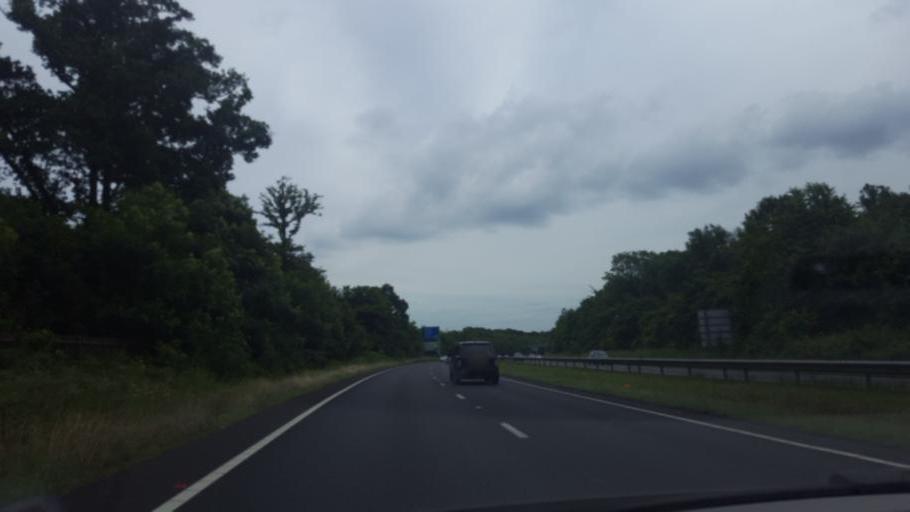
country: GB
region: England
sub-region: Royal Borough of Windsor and Maidenhead
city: Bisham
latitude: 51.5234
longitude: -0.7701
